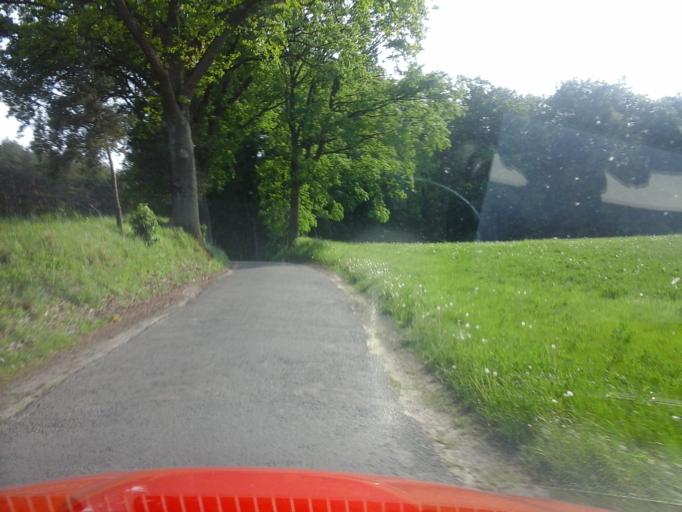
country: PL
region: West Pomeranian Voivodeship
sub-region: Powiat mysliborski
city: Barlinek
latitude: 53.0249
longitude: 15.2232
